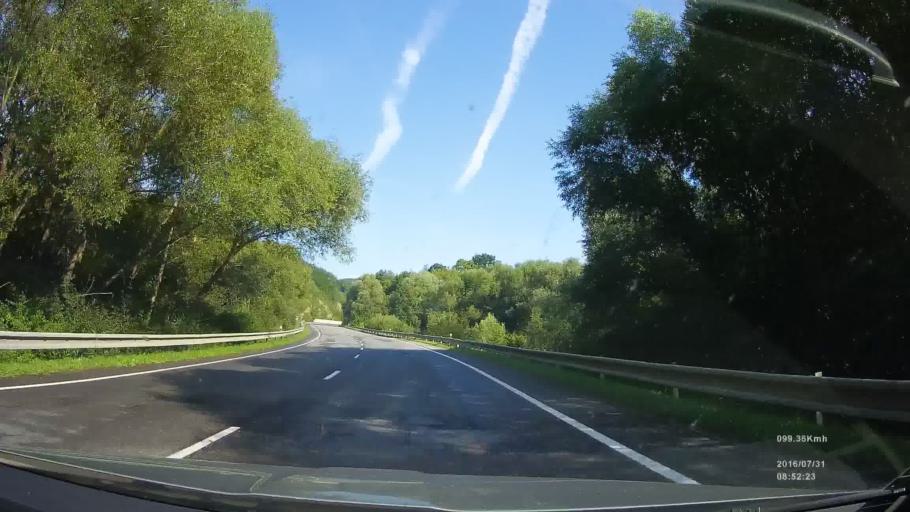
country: SK
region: Presovsky
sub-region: Okres Presov
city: Presov
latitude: 49.1133
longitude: 21.3153
